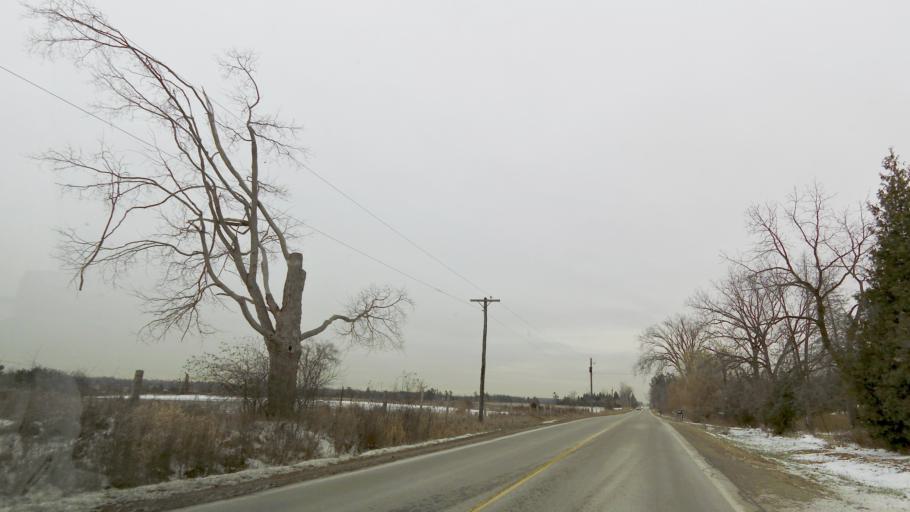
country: CA
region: Ontario
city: Vaughan
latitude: 43.8628
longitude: -79.5917
